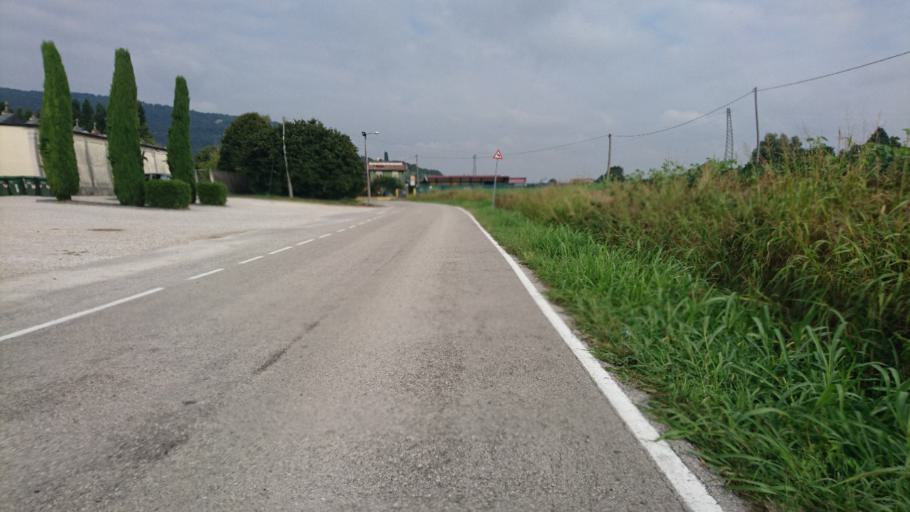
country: IT
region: Veneto
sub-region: Provincia di Vicenza
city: Longare
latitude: 45.4669
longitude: 11.6157
